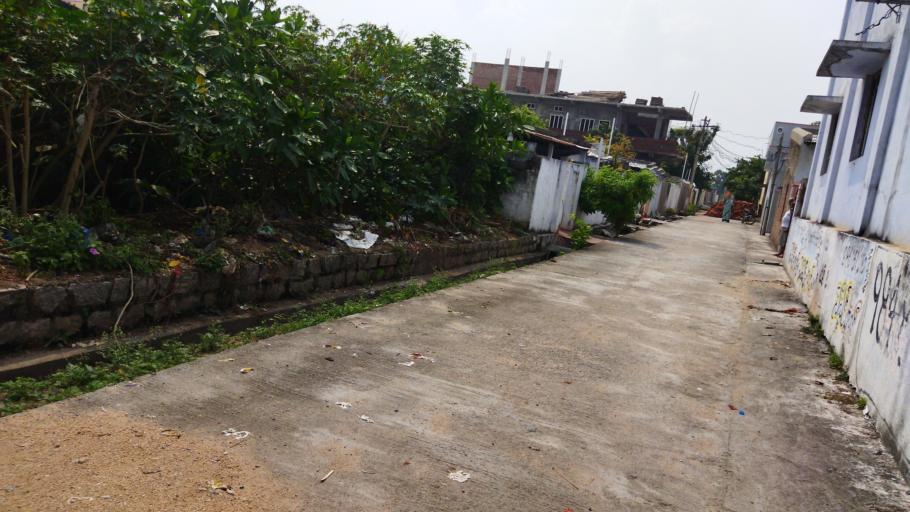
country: IN
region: Telangana
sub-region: Nalgonda
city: Nalgonda
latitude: 17.1678
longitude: 79.4181
